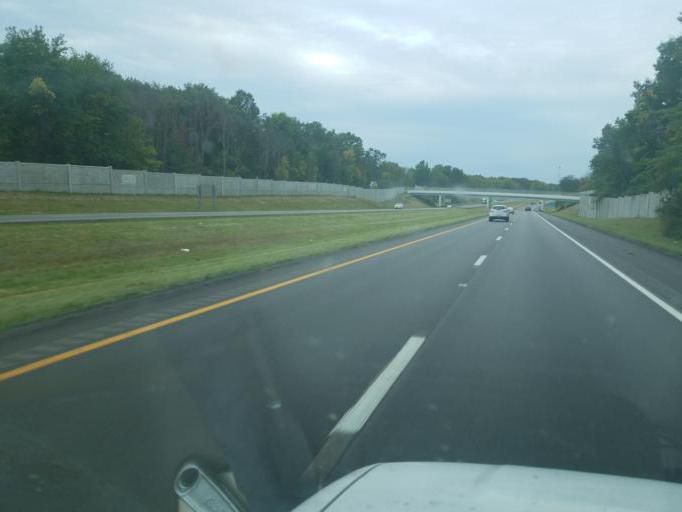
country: US
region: Ohio
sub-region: Mahoning County
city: Craig Beach
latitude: 41.1021
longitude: -80.9678
